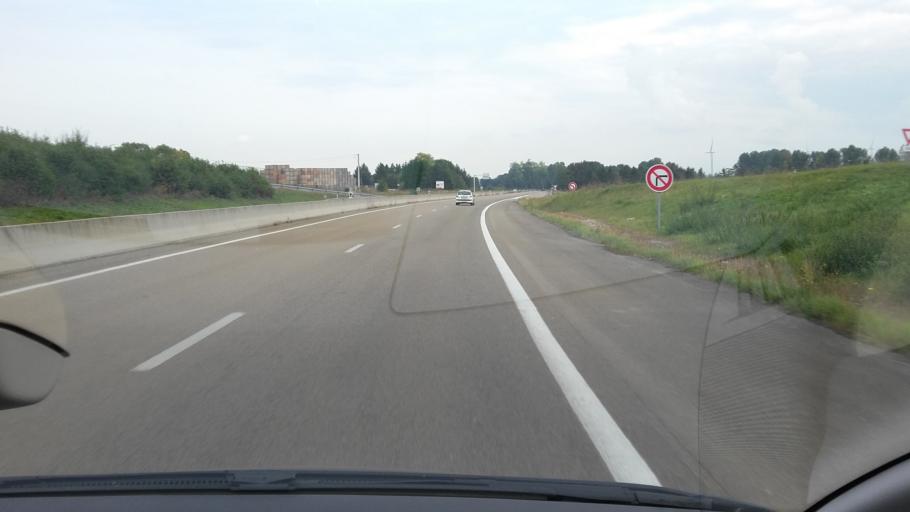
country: FR
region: Champagne-Ardenne
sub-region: Departement de la Marne
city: Fere-Champenoise
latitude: 48.7450
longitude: 3.9678
